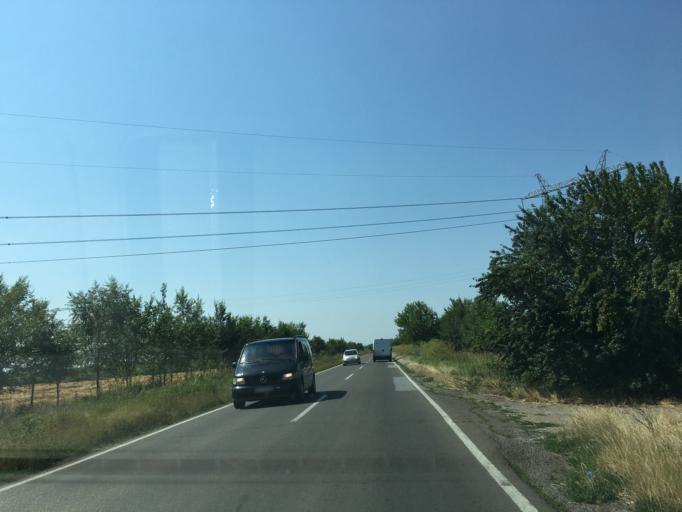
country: RS
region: Central Serbia
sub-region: Belgrade
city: Grocka
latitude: 44.7876
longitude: 20.7236
